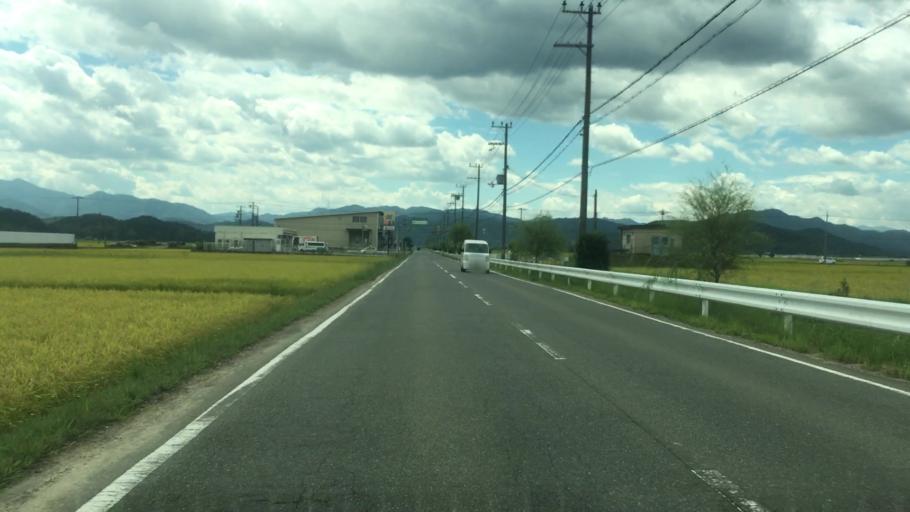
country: JP
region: Hyogo
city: Toyooka
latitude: 35.5265
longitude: 134.8398
